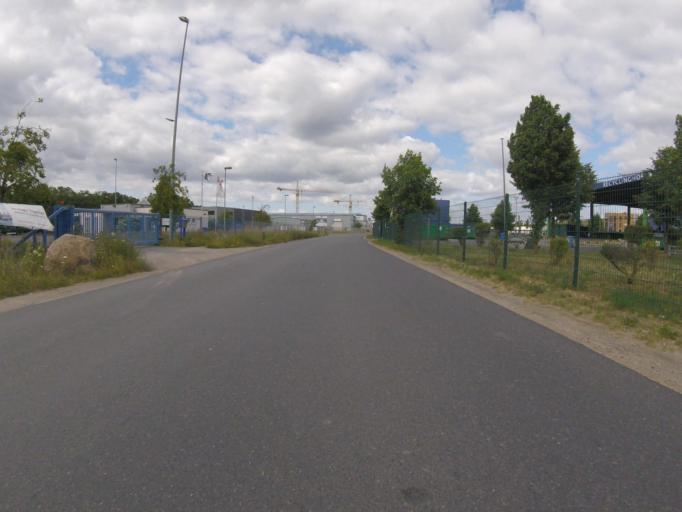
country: DE
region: Brandenburg
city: Wildau
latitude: 52.3172
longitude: 13.6707
